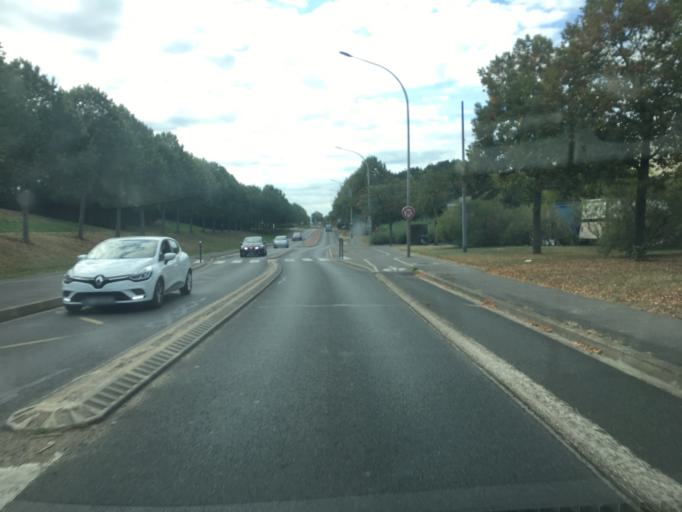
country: FR
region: Ile-de-France
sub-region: Departement du Val-de-Marne
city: Valenton
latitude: 48.7479
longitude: 2.4601
